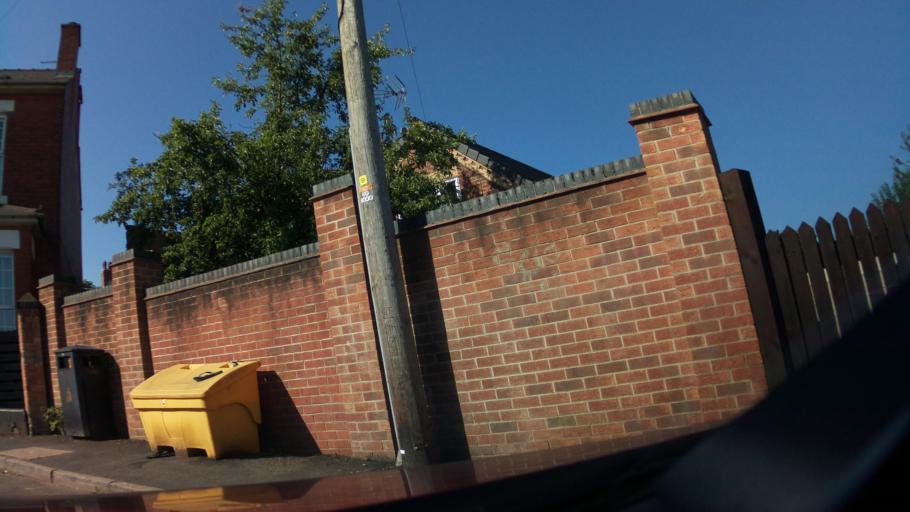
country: GB
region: England
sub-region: Derby
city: Derby
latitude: 52.9182
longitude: -1.4980
